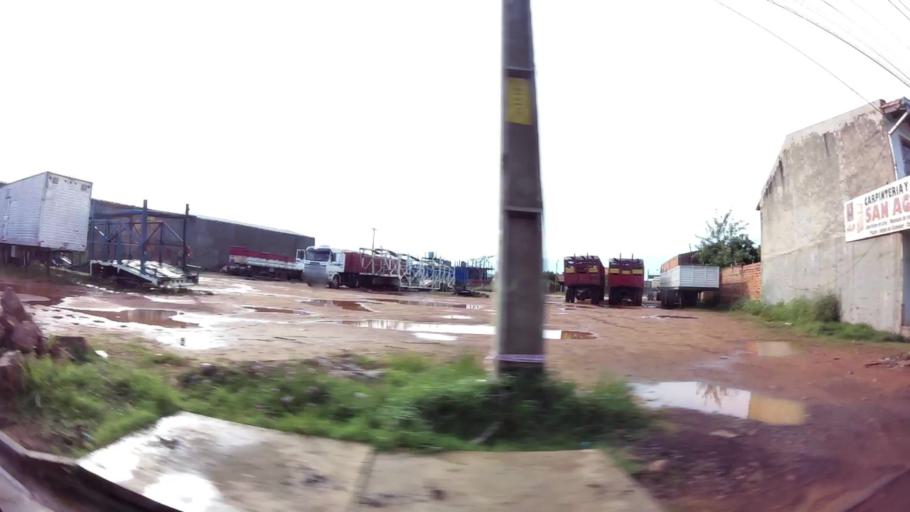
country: PY
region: Central
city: Limpio
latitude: -25.1854
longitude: -57.4944
